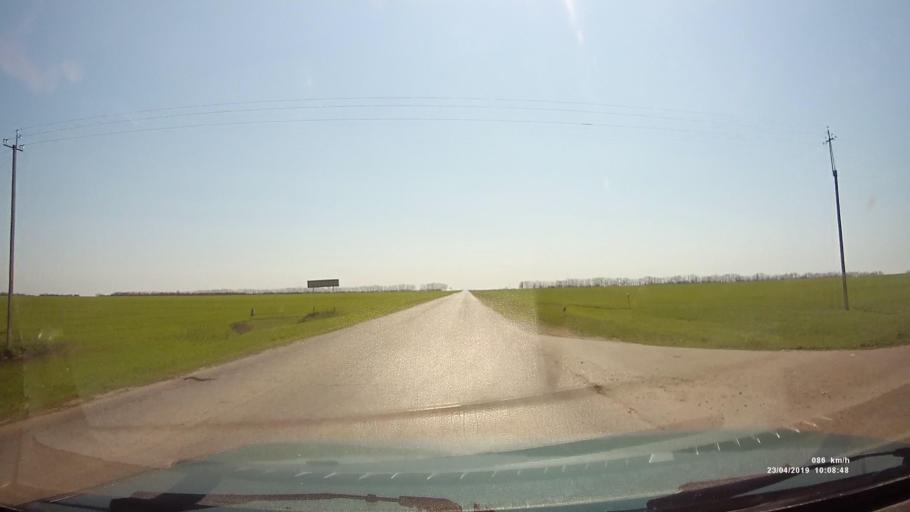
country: RU
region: Rostov
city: Sovetskoye
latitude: 46.7168
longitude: 42.2708
